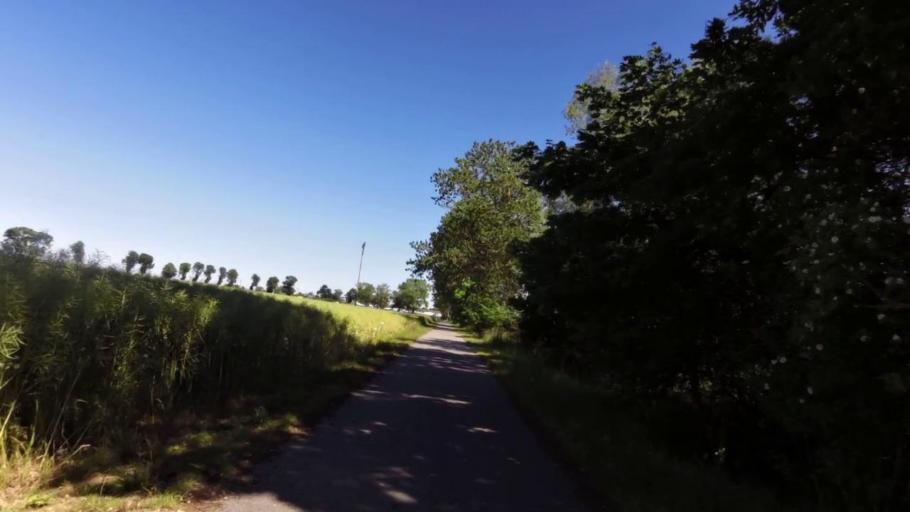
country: PL
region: West Pomeranian Voivodeship
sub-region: Powiat kolobrzeski
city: Dygowo
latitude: 54.0465
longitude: 15.7463
